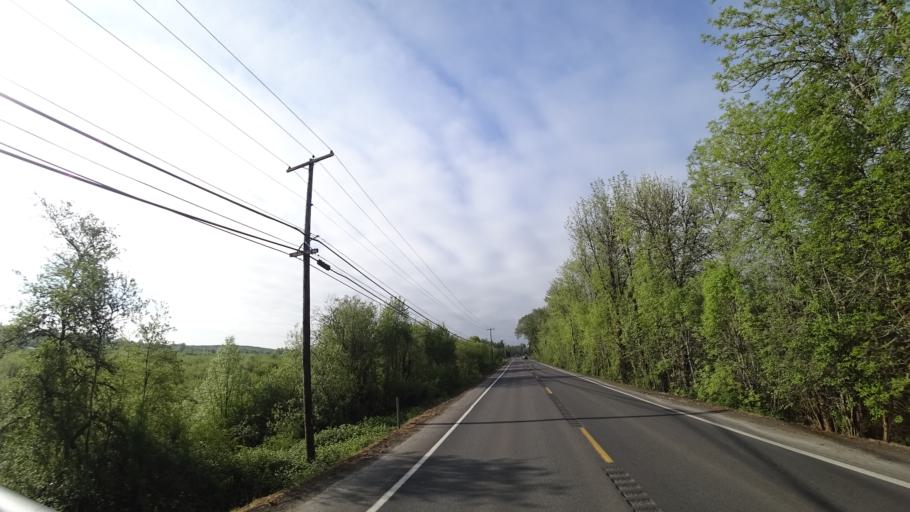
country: US
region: Oregon
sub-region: Washington County
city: Hillsboro
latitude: 45.5050
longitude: -122.9910
